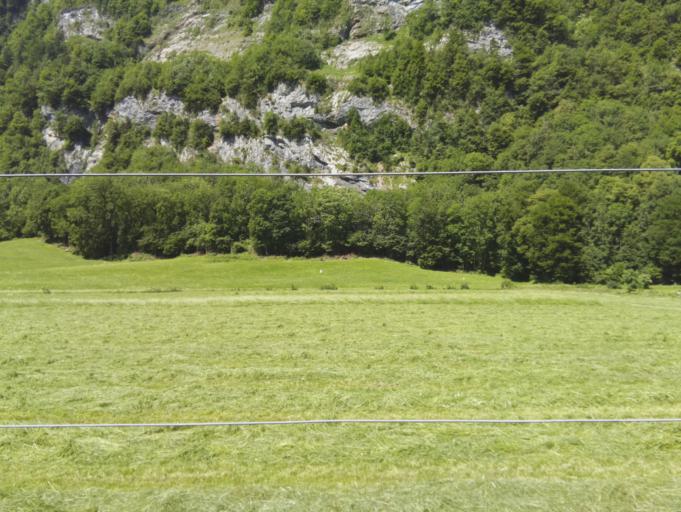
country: CH
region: Glarus
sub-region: Glarus
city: Netstal
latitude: 47.0813
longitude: 9.0552
